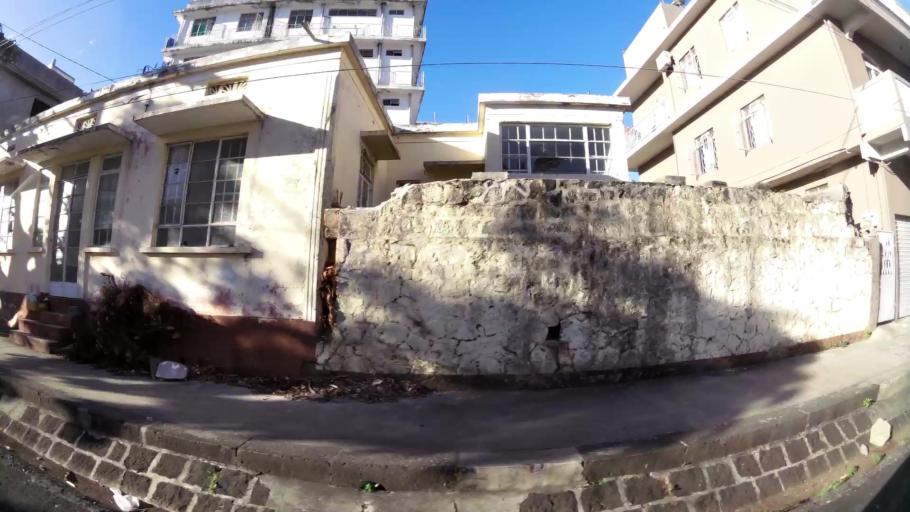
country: MU
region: Port Louis
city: Port Louis
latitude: -20.1693
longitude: 57.5063
